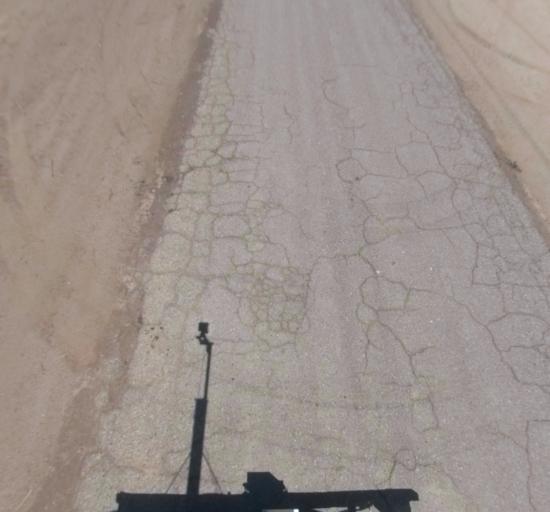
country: US
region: California
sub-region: Madera County
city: Chowchilla
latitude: 37.0009
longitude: -120.3285
